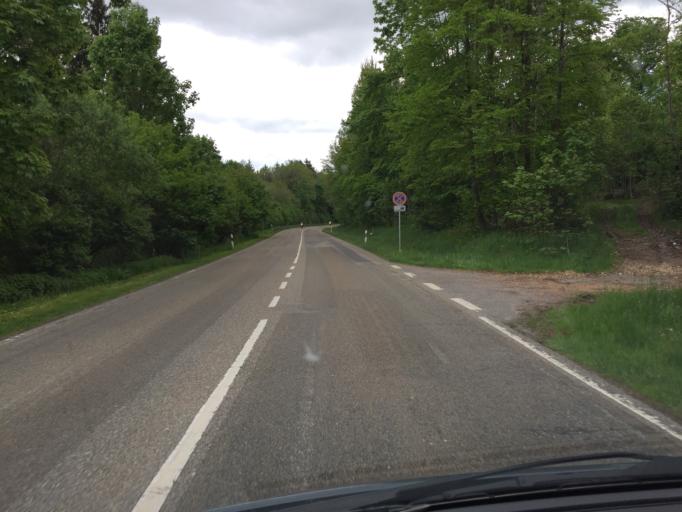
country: DE
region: Baden-Wuerttemberg
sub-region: Freiburg Region
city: Monchweiler
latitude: 48.0664
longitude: 8.4353
